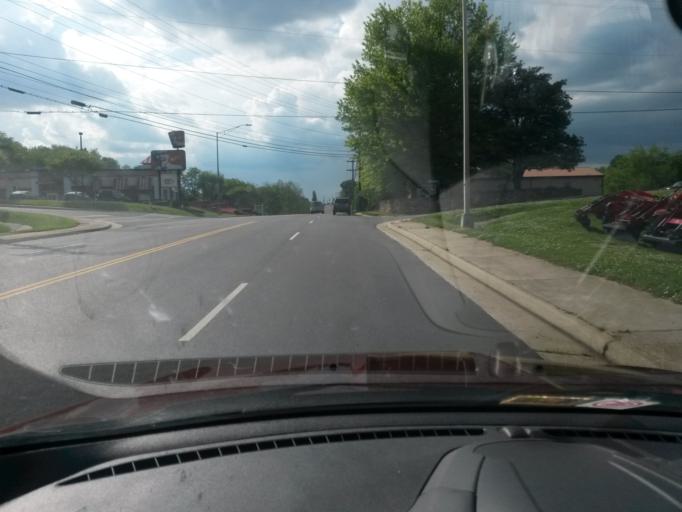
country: US
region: Virginia
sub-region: City of Bedford
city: Bedford
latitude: 37.3290
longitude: -79.5090
